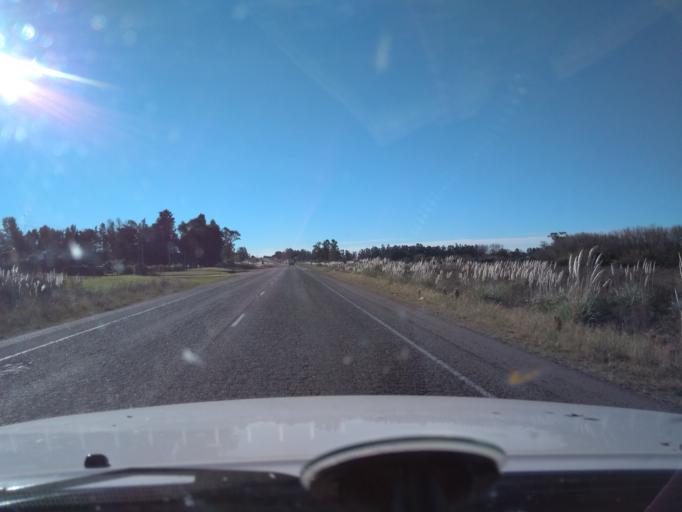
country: UY
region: Canelones
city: Sauce
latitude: -34.5989
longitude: -56.0505
